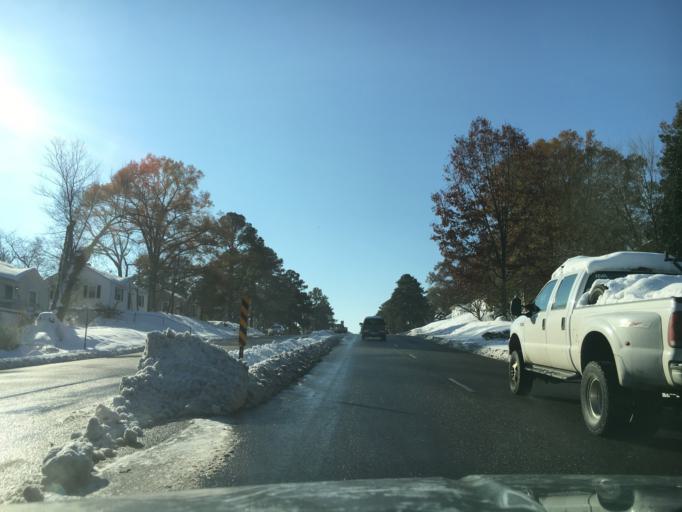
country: US
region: Virginia
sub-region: Henrico County
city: Tuckahoe
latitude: 37.6012
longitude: -77.5284
